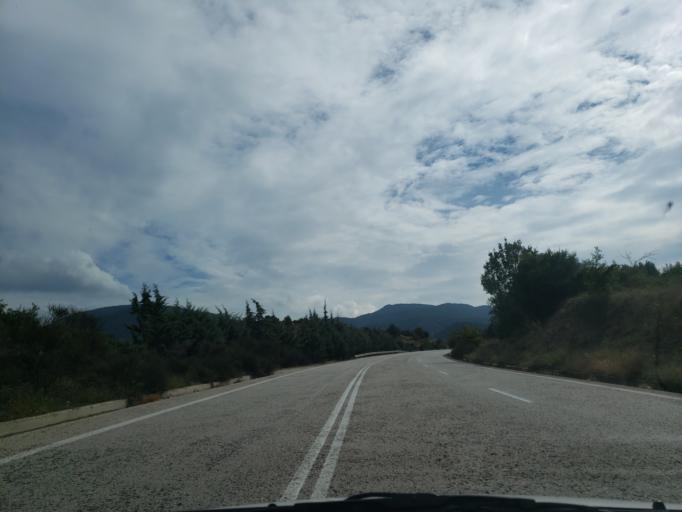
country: GR
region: Central Greece
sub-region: Nomos Fthiotidos
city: Domokos
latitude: 39.0245
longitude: 22.3714
